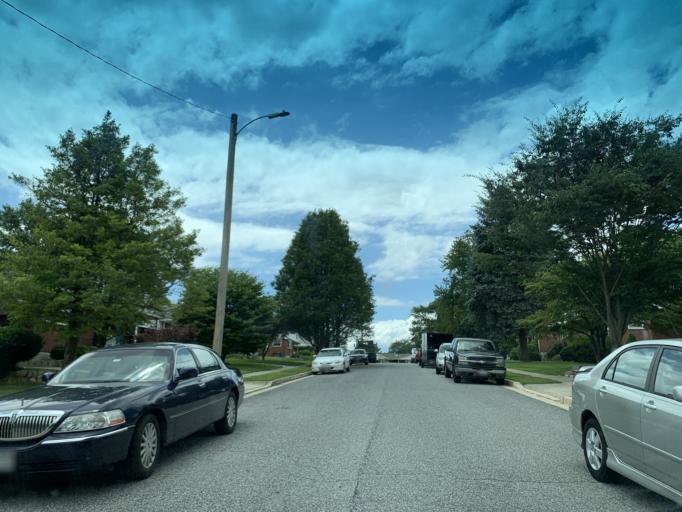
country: US
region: Maryland
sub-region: Baltimore County
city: Timonium
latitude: 39.4421
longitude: -76.6203
